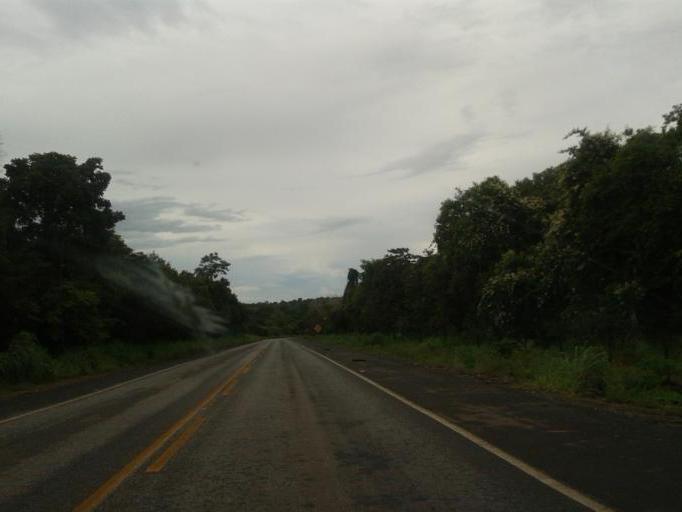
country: BR
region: Goias
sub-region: Mozarlandia
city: Mozarlandia
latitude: -14.8363
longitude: -50.5389
